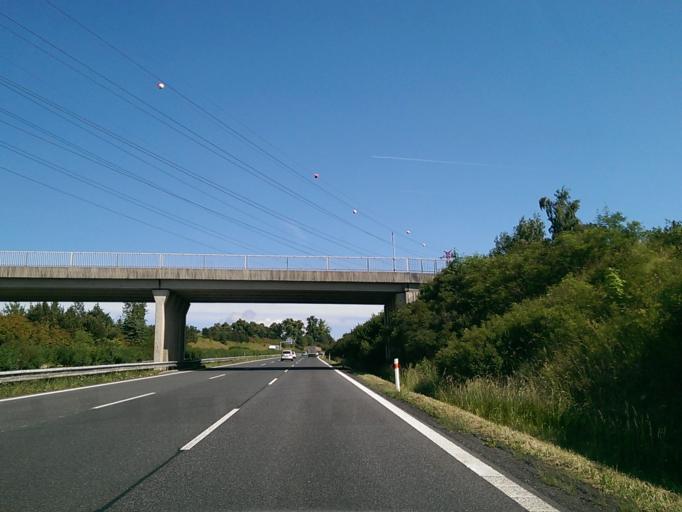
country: CZ
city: Ohrazenice
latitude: 50.6215
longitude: 15.1093
